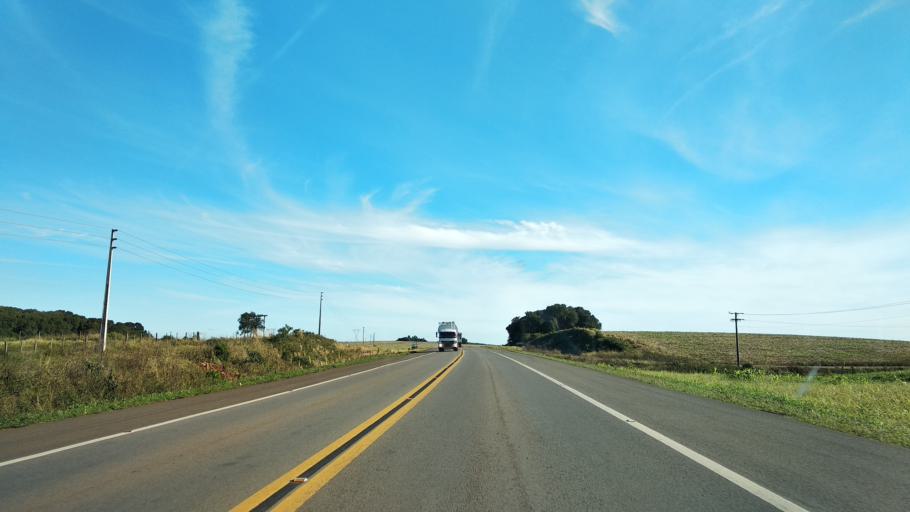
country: BR
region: Santa Catarina
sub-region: Celso Ramos
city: Celso Ramos
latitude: -27.4955
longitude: -51.3380
